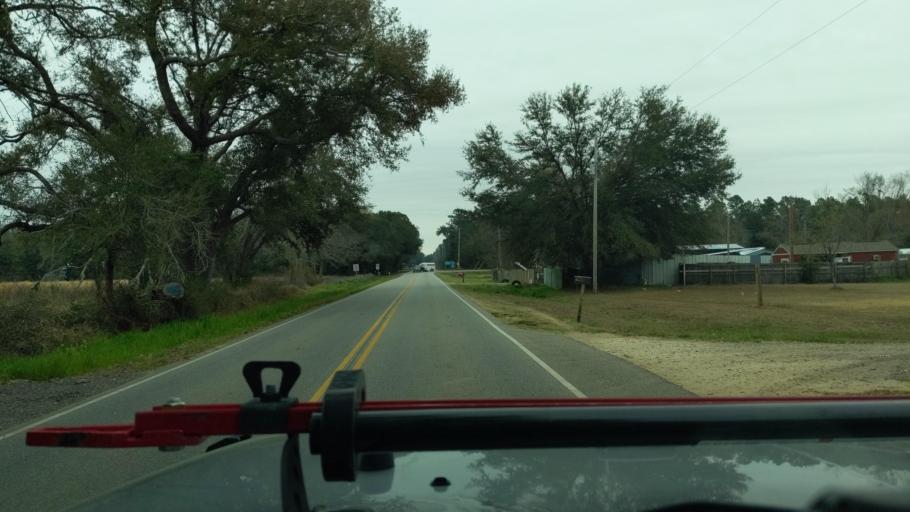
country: US
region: Alabama
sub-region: Baldwin County
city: Foley
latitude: 30.4579
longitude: -87.7783
